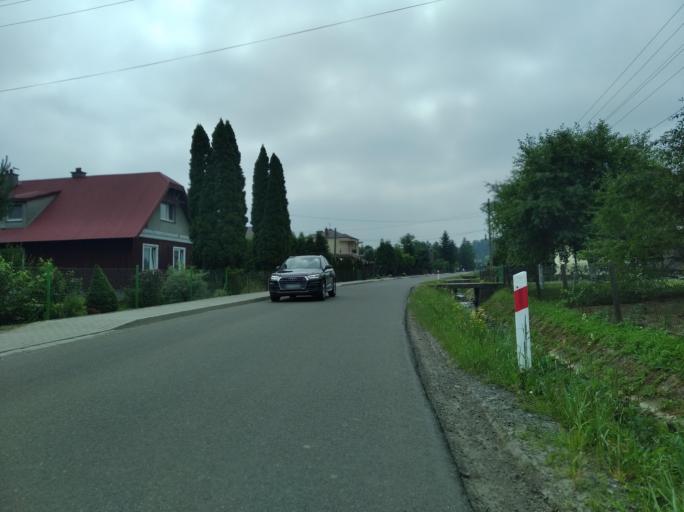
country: PL
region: Subcarpathian Voivodeship
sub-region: Powiat sanocki
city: Besko
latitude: 49.5925
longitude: 21.9408
